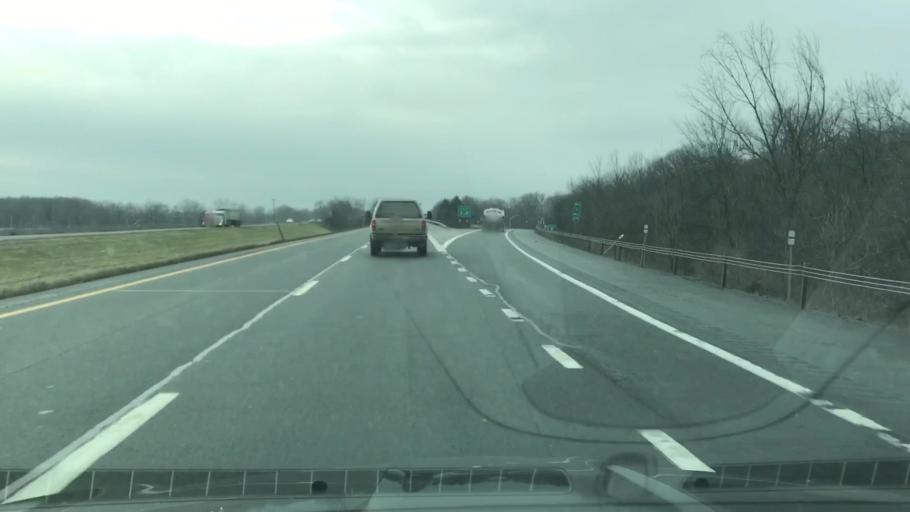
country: US
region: New York
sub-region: Orange County
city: Maybrook
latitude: 41.5129
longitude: -74.2029
